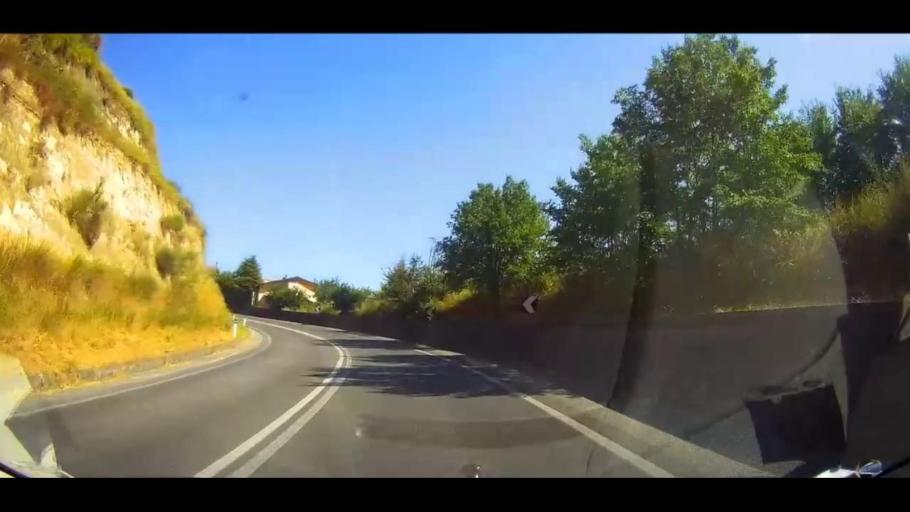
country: IT
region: Calabria
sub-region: Provincia di Cosenza
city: Cosenza
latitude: 39.2967
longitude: 16.2640
